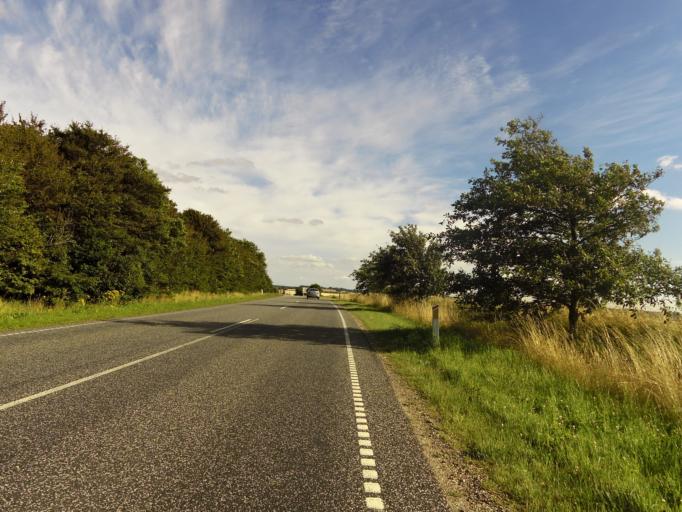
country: DK
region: South Denmark
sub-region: Tonder Kommune
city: Toftlund
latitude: 55.1838
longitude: 9.0595
